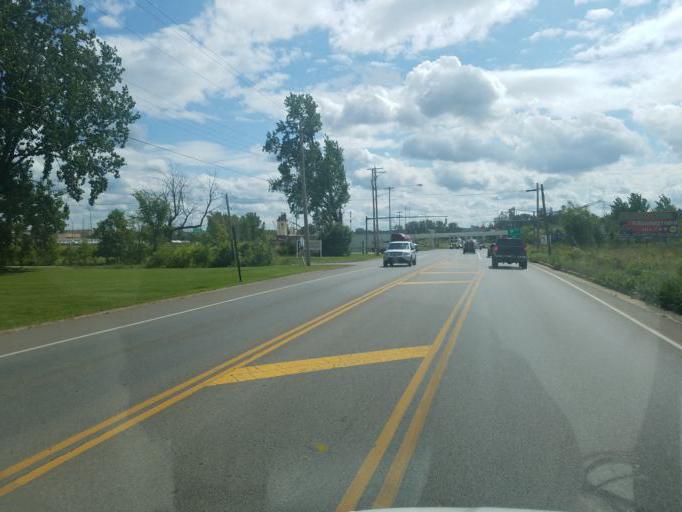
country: US
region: Ohio
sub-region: Richland County
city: Mansfield
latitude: 40.7807
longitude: -82.5139
